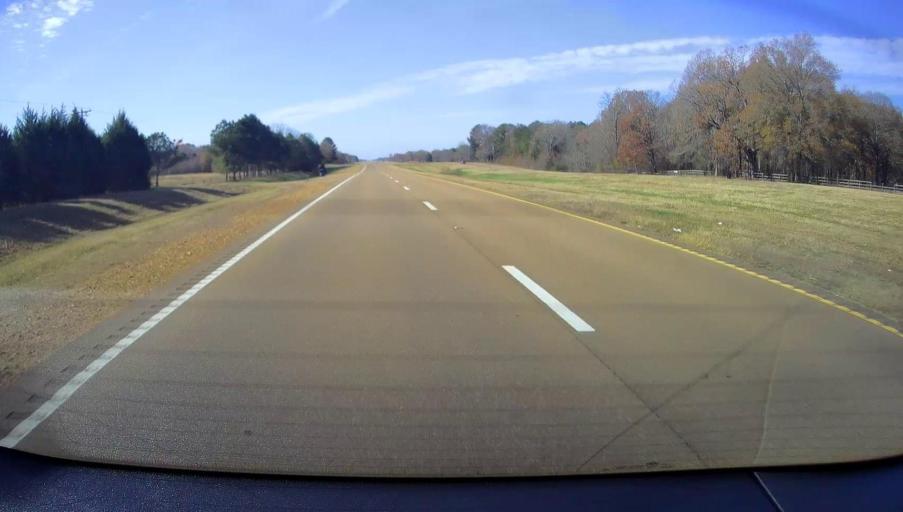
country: US
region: Mississippi
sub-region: Marshall County
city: Holly Springs
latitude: 34.9460
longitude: -89.3495
